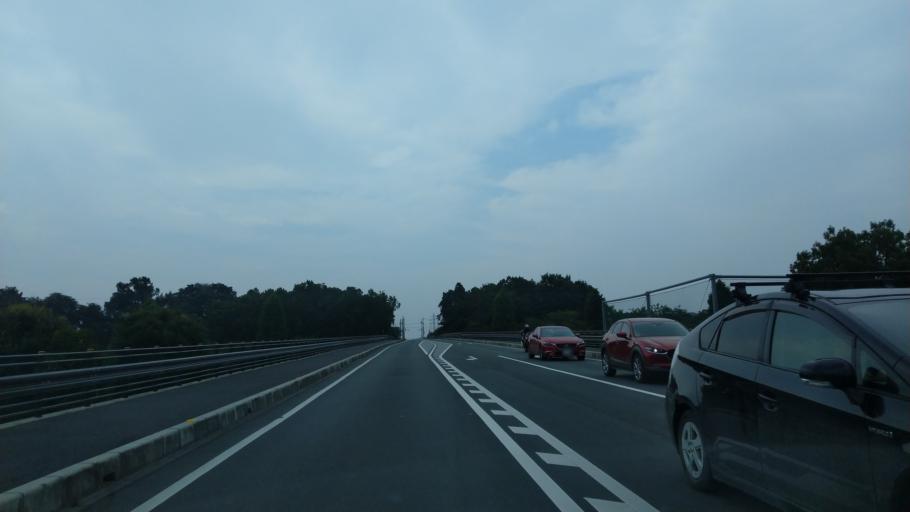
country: JP
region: Saitama
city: Morohongo
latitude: 35.9106
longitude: 139.3262
